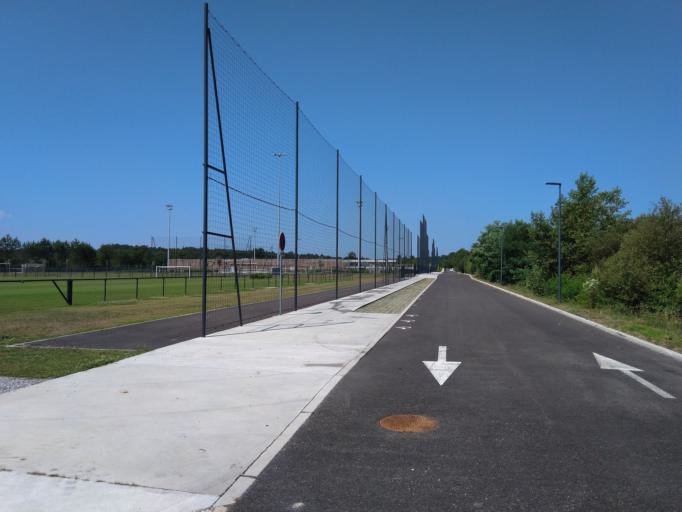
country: FR
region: Aquitaine
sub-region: Departement des Landes
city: Saint-Paul-les-Dax
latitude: 43.7384
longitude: -1.0879
